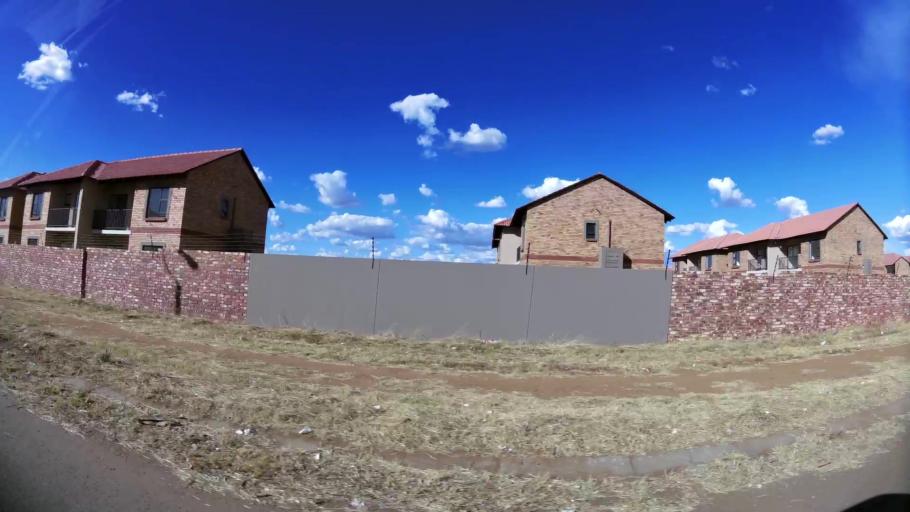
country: ZA
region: North-West
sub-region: Dr Kenneth Kaunda District Municipality
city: Klerksdorp
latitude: -26.8235
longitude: 26.6574
